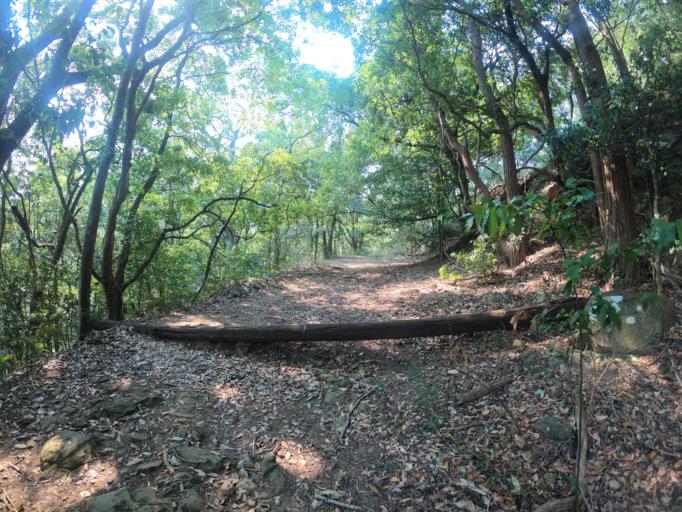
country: AU
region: New South Wales
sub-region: Wollongong
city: Bulli
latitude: -34.3258
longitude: 150.8885
